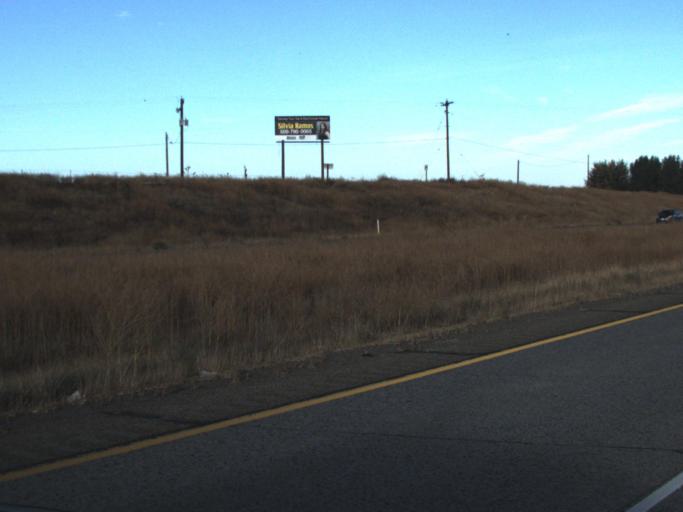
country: US
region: Washington
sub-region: Yakima County
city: Grandview
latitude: 46.2788
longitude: -119.9352
